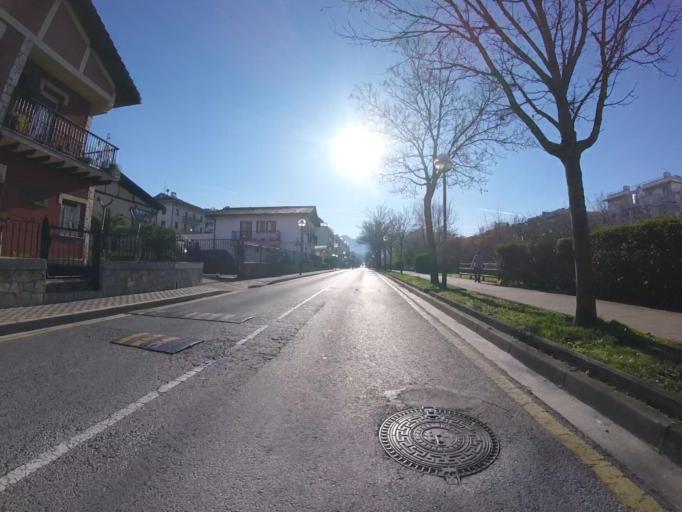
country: ES
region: Basque Country
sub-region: Provincia de Guipuzcoa
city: Irun
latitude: 43.3397
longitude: -1.7783
